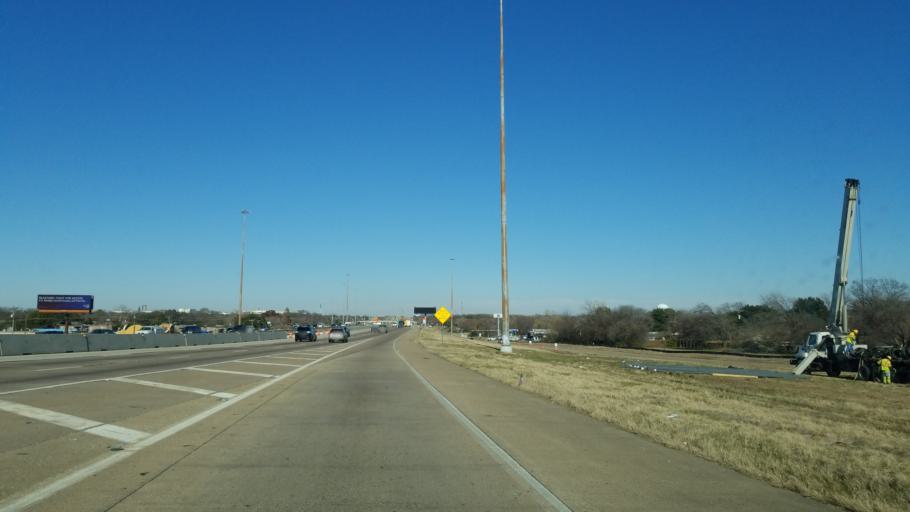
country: US
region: Texas
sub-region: Tarrant County
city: Arlington
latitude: 32.7174
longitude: -97.0625
